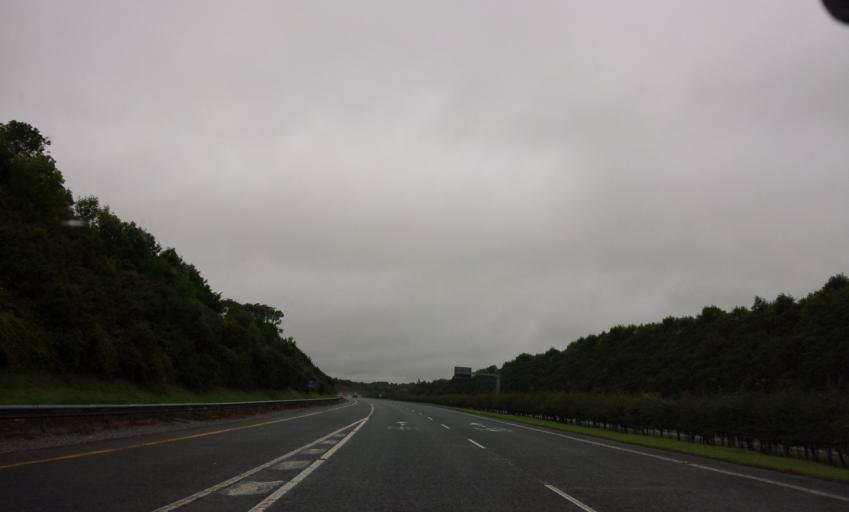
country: IE
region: Munster
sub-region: County Cork
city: Watergrasshill
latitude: 51.9584
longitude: -8.3874
